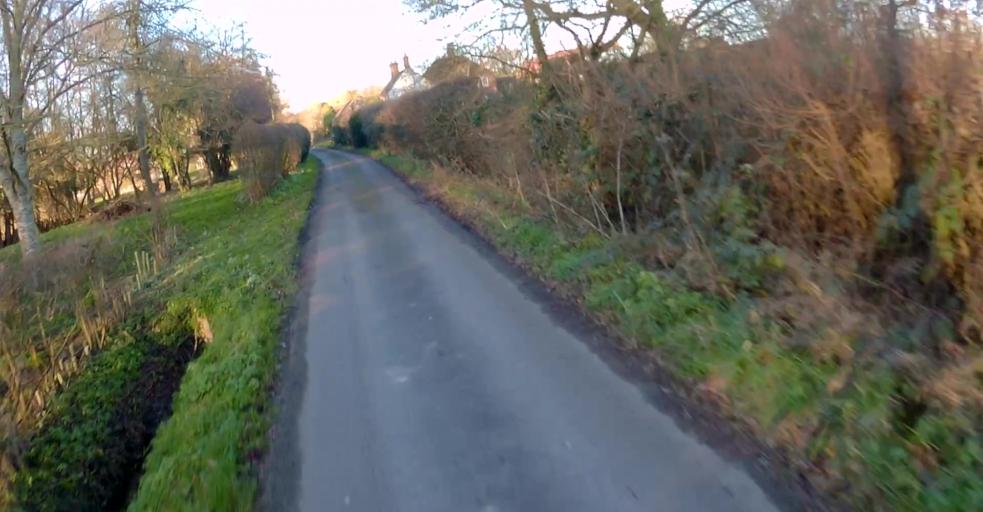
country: GB
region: England
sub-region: Hampshire
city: Hook
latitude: 51.3089
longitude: -1.0013
